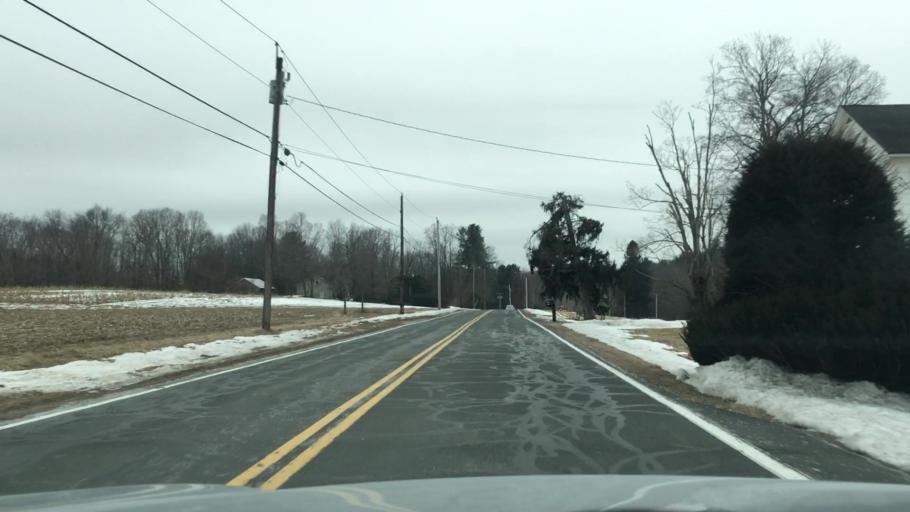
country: US
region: Massachusetts
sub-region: Hampden County
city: Westfield
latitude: 42.0804
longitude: -72.7203
